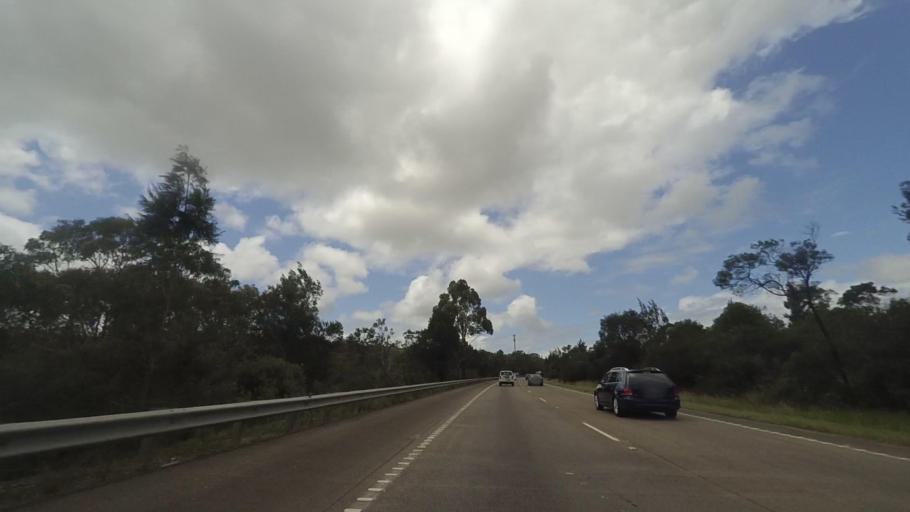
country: AU
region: New South Wales
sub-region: Gosford Shire
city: Narara
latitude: -33.3782
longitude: 151.3013
